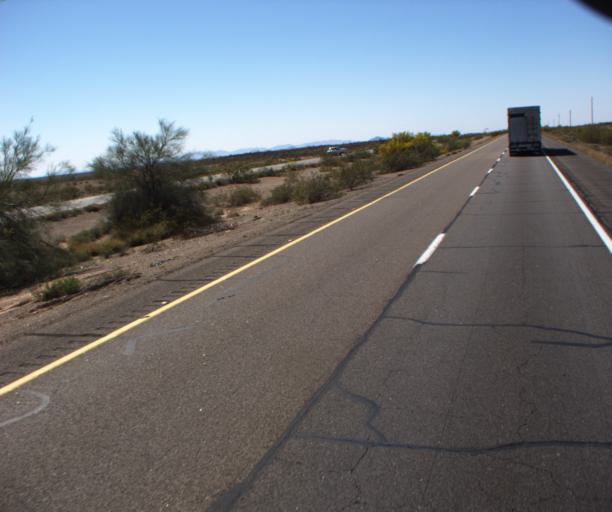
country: US
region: Arizona
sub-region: Maricopa County
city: Gila Bend
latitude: 32.8566
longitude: -113.2354
